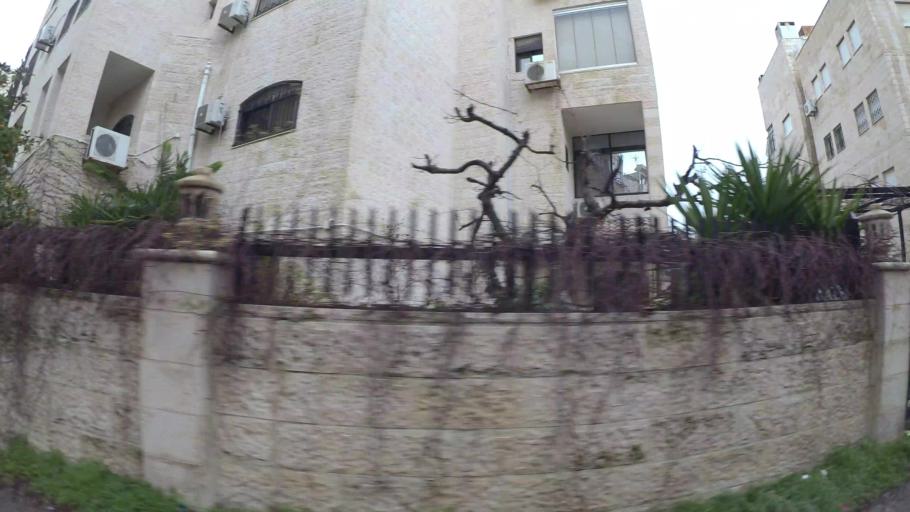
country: JO
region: Amman
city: Wadi as Sir
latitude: 31.9661
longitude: 35.8636
